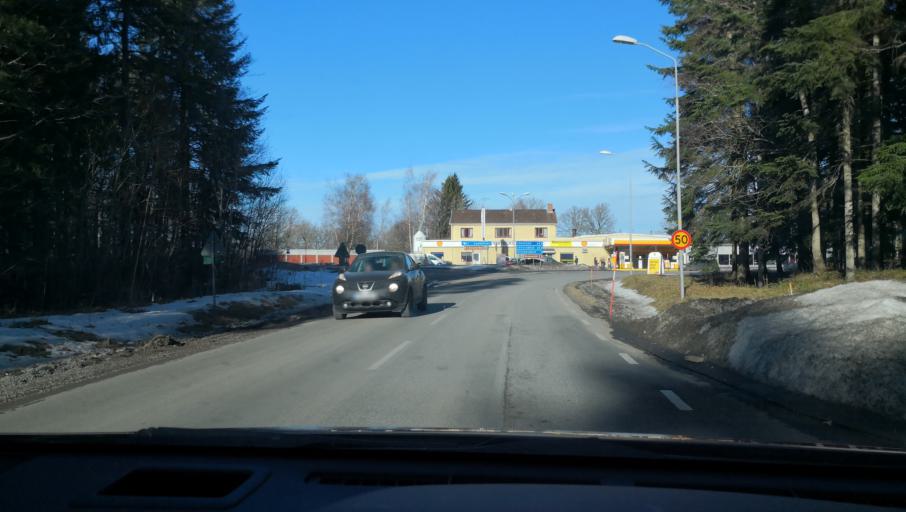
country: SE
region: Uppsala
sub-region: Osthammars Kommun
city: Osterbybruk
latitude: 60.1967
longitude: 17.8781
